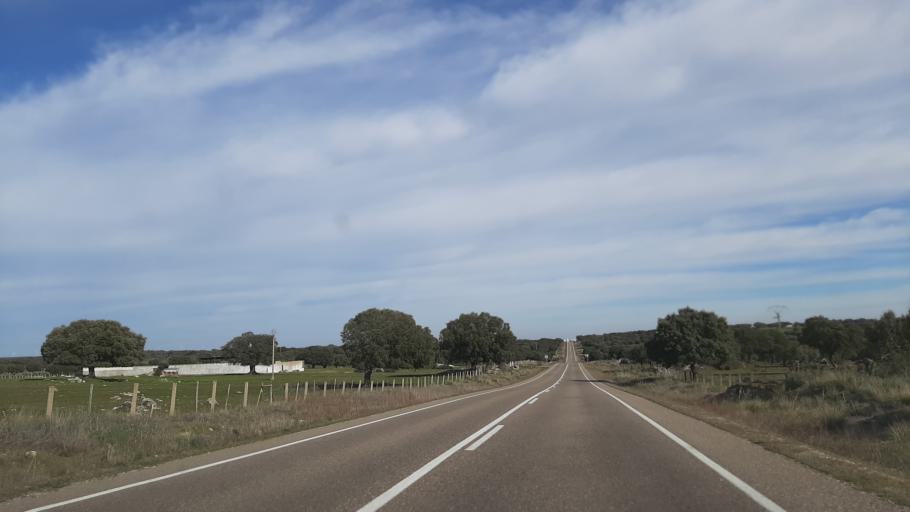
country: ES
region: Castille and Leon
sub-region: Provincia de Salamanca
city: Ledesma
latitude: 41.0900
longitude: -5.9628
